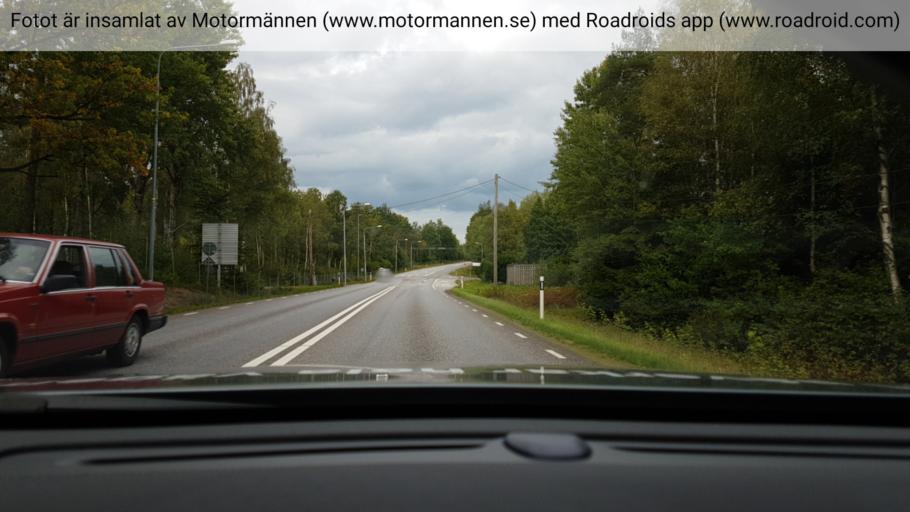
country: SE
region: Halland
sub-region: Hylte Kommun
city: Hyltebruk
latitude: 56.9904
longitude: 13.2187
